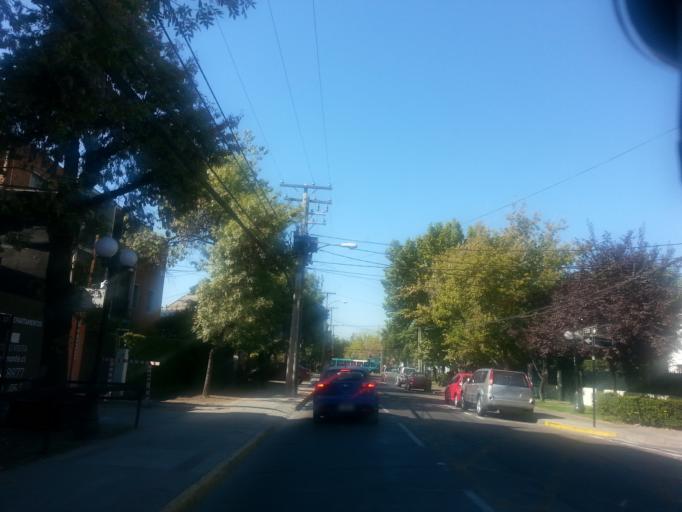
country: CL
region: Santiago Metropolitan
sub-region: Provincia de Santiago
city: Villa Presidente Frei, Nunoa, Santiago, Chile
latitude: -33.4348
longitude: -70.5958
